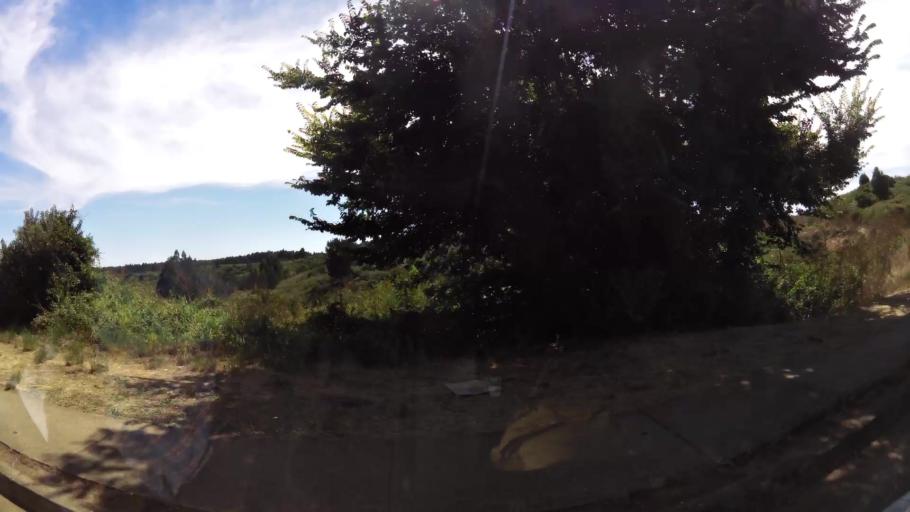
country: CL
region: Biobio
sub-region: Provincia de Concepcion
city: Talcahuano
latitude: -36.7095
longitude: -73.1268
